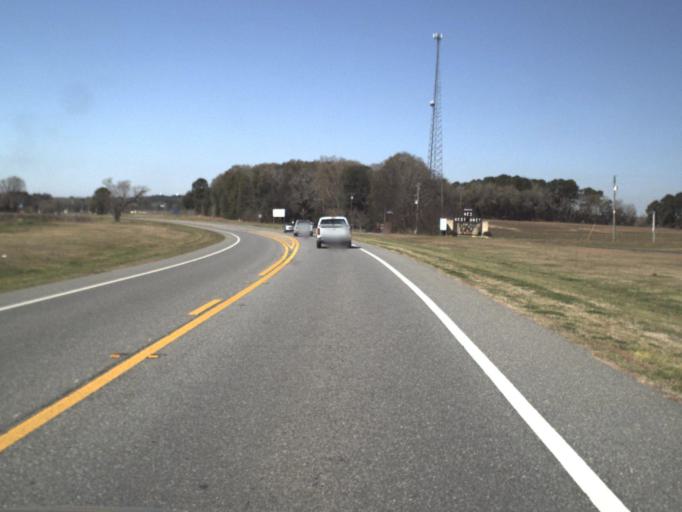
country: US
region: Florida
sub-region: Jackson County
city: Sneads
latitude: 30.7080
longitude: -84.8960
